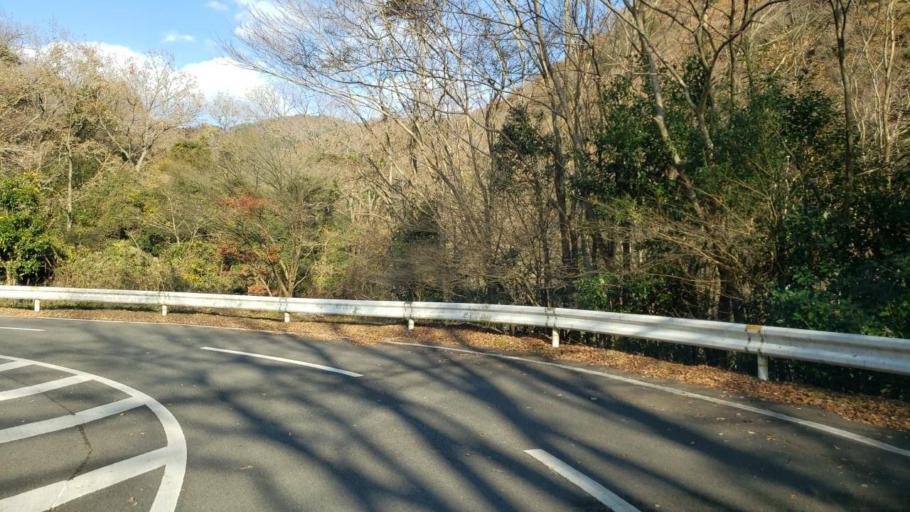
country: JP
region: Tokushima
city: Wakimachi
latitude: 34.1006
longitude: 134.0733
